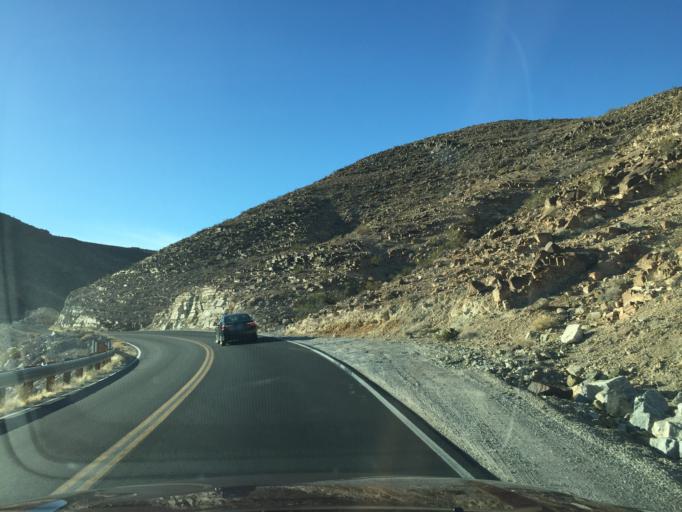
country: US
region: California
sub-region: Inyo County
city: Lone Pine
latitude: 36.3482
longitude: -117.5377
